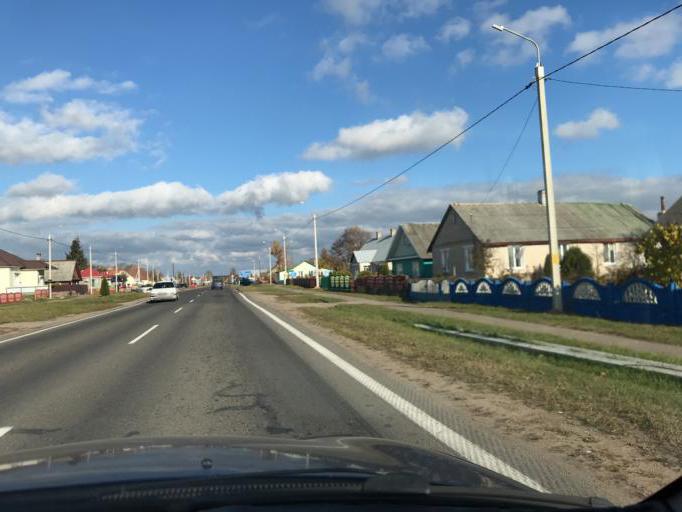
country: LT
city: Salcininkai
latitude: 54.2483
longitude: 25.3559
